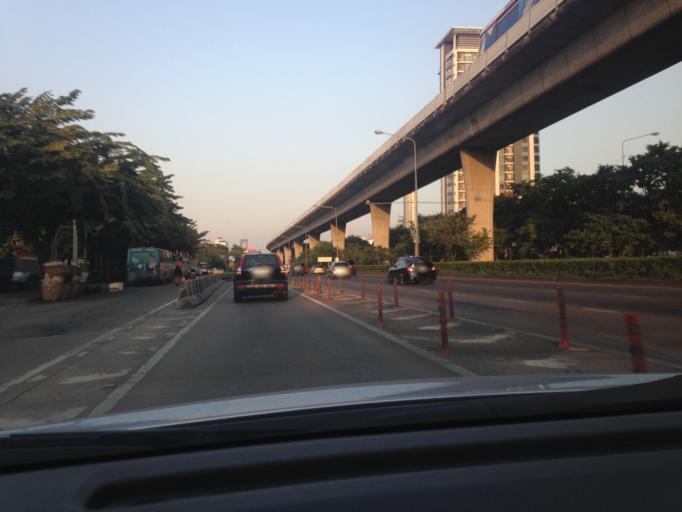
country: TH
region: Bangkok
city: Bangkok Yai
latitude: 13.7173
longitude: 100.4811
